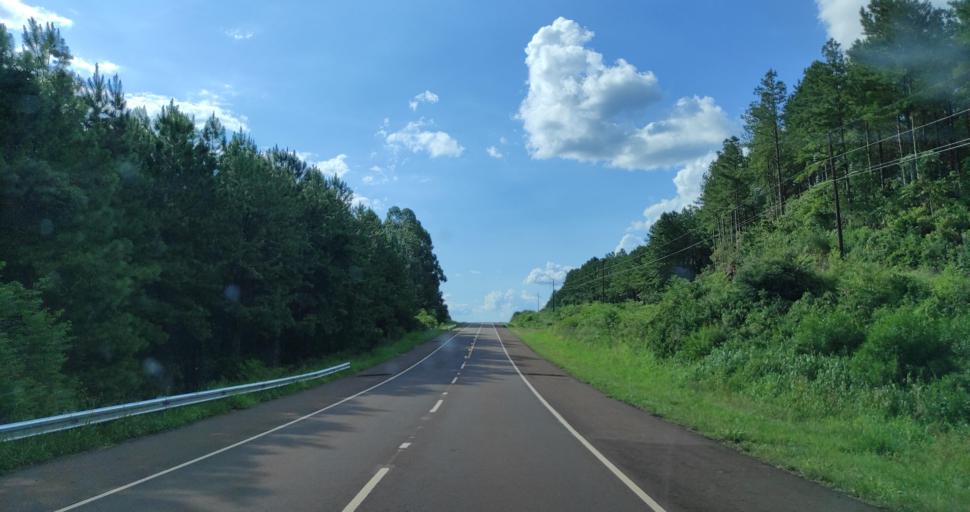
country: AR
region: Misiones
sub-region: Departamento de San Pedro
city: San Pedro
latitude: -26.3639
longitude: -53.9492
